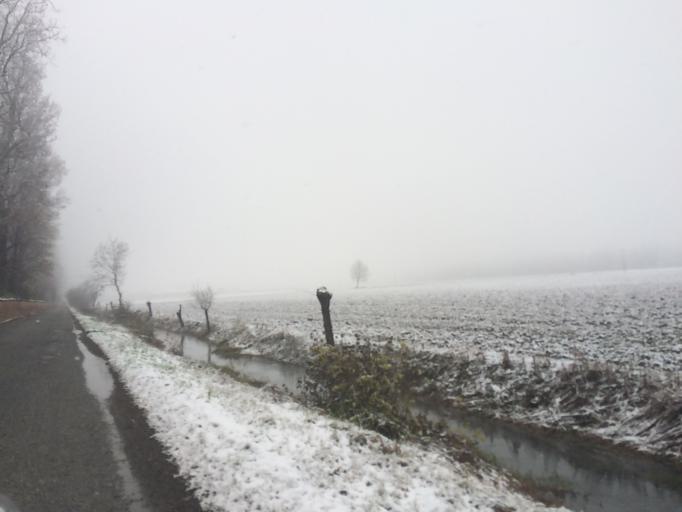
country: IT
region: Piedmont
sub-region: Provincia di Cuneo
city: Racconigi
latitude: 44.7854
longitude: 7.6668
